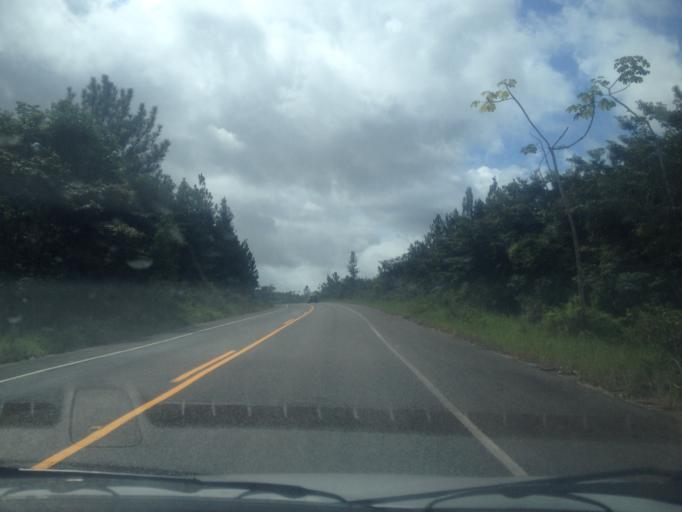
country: BR
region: Bahia
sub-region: Entre Rios
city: Entre Rios
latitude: -12.1443
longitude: -37.7937
